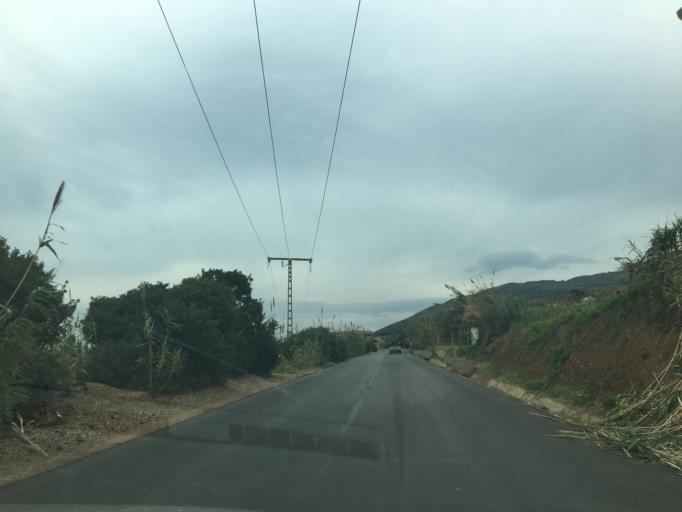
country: DZ
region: Tipaza
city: Tipasa
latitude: 36.6390
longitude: 2.3280
